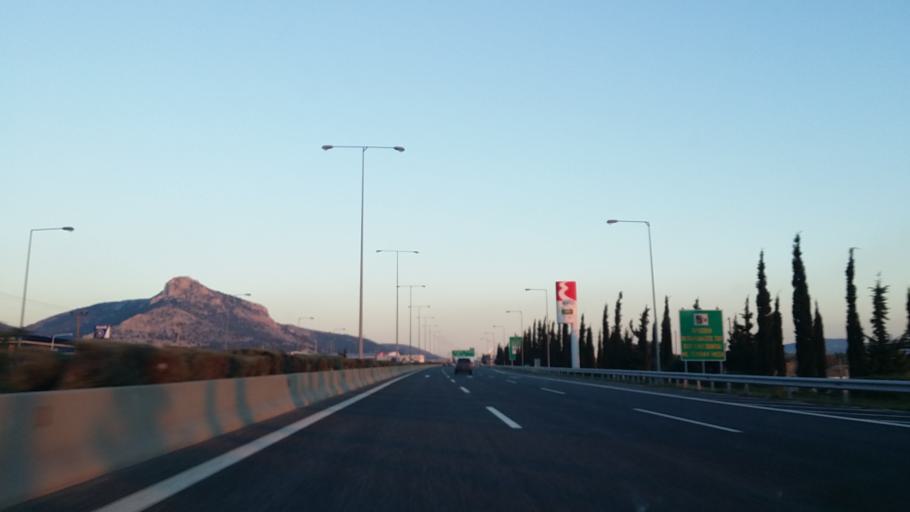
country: GR
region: Attica
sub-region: Nomarchia Dytikis Attikis
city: Aspropyrgos
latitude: 38.0937
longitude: 23.5993
